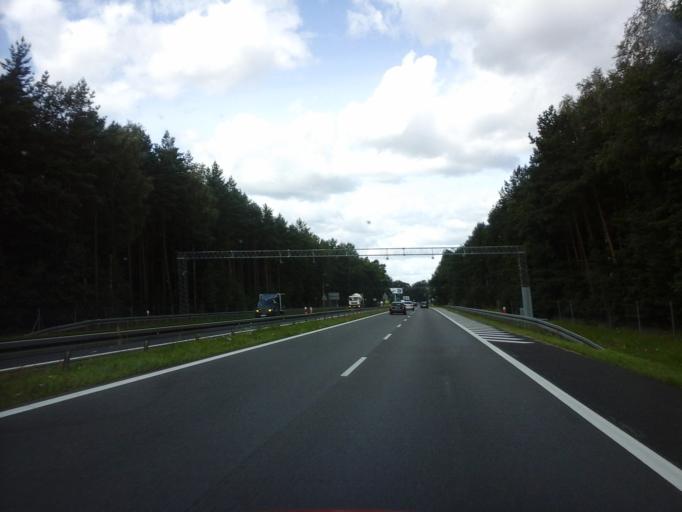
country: PL
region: West Pomeranian Voivodeship
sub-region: Powiat gryfinski
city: Stare Czarnowo
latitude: 53.3608
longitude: 14.7628
